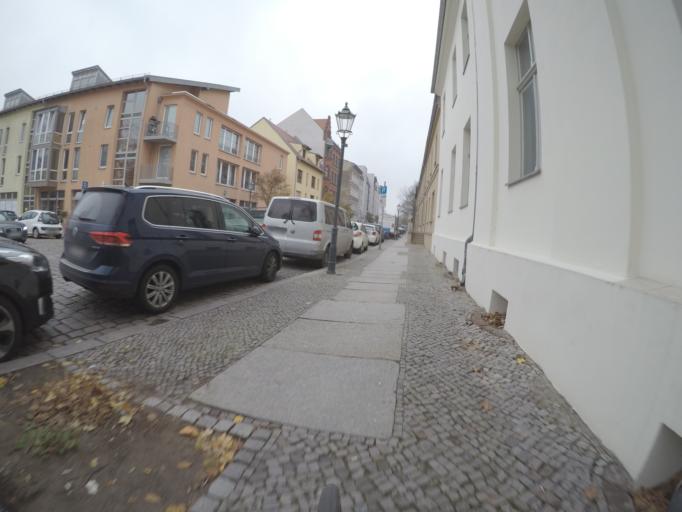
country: DE
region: Berlin
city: Kopenick Bezirk
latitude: 52.4474
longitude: 13.5782
